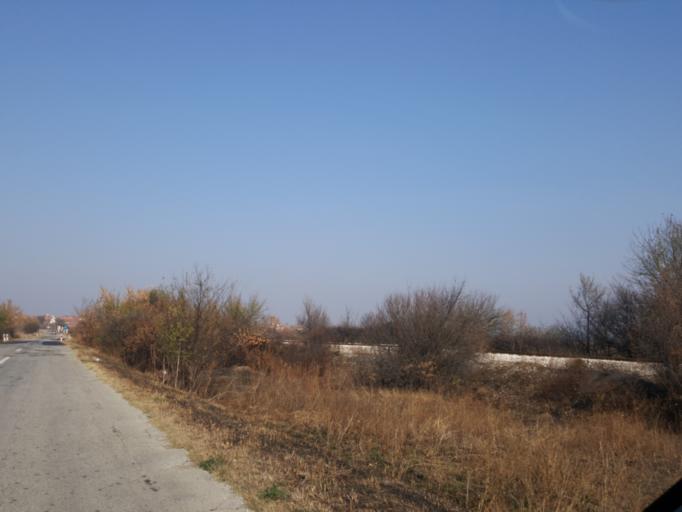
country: BG
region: Vidin
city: Bregovo
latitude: 44.1832
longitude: 22.5945
